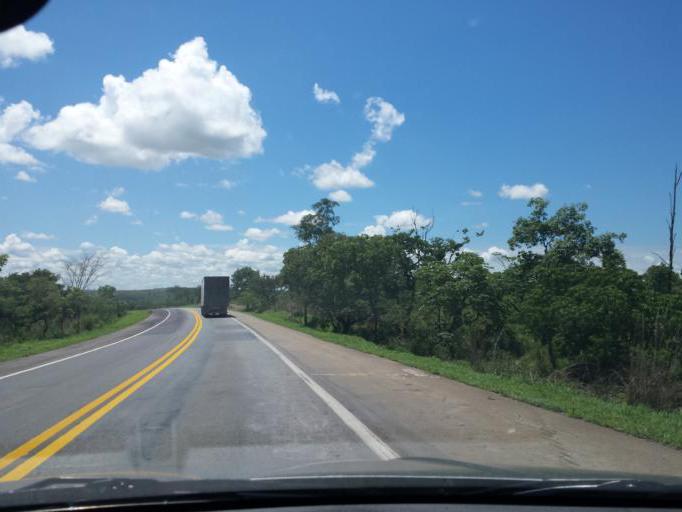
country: BR
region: Goias
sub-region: Luziania
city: Luziania
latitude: -16.5260
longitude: -47.8084
